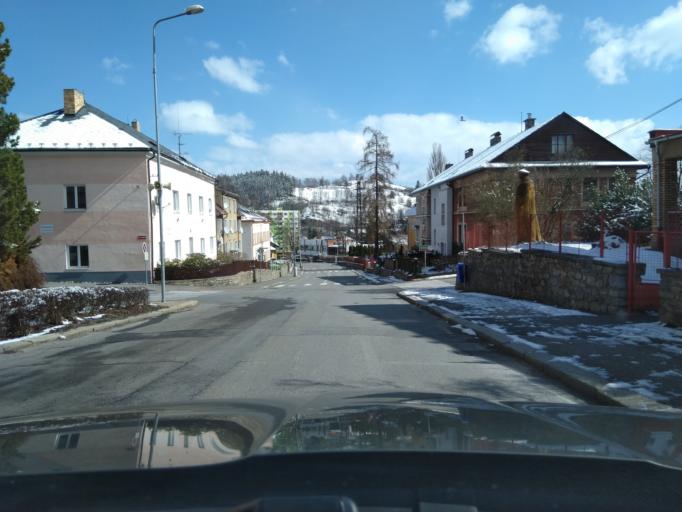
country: CZ
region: Jihocesky
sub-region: Okres Prachatice
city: Vimperk
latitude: 49.0555
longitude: 13.7798
